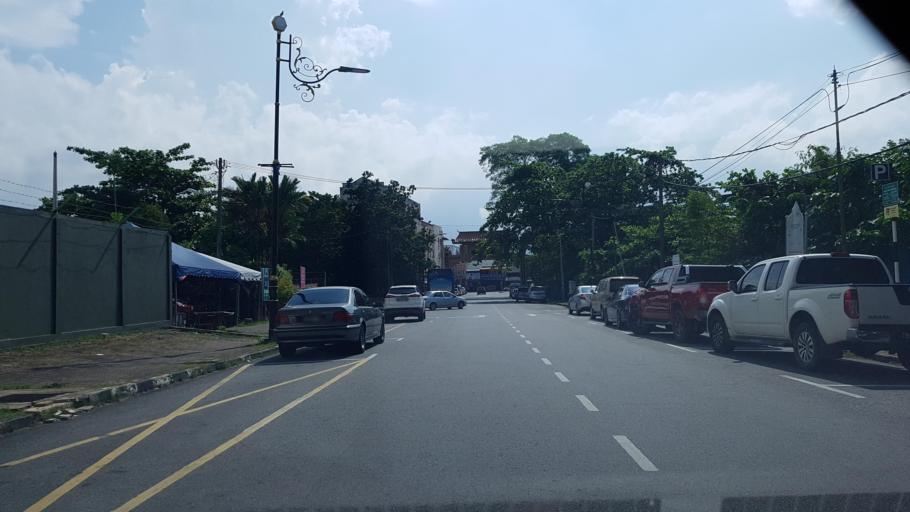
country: MY
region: Terengganu
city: Kuala Terengganu
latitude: 5.3322
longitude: 103.1344
